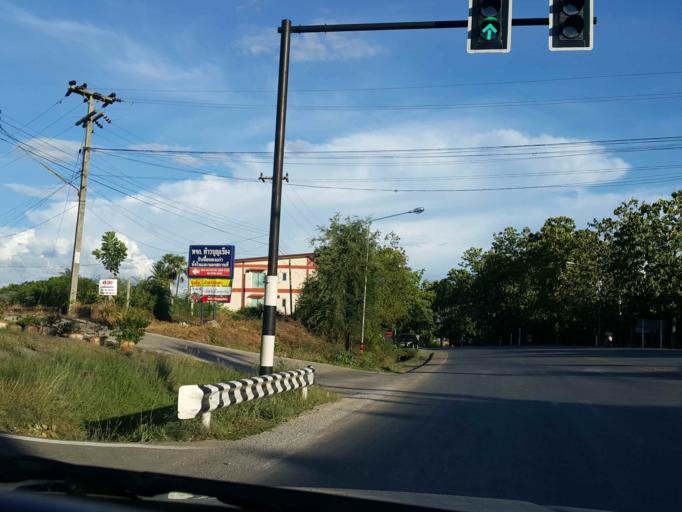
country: TH
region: Chiang Mai
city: Chom Thong
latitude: 18.4374
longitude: 98.6797
